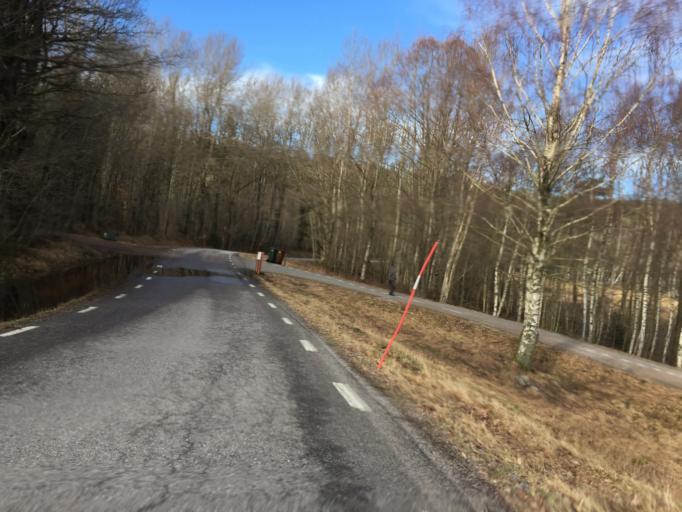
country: SE
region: Vaestra Goetaland
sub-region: Kungalvs Kommun
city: Kungalv
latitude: 57.9287
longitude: 11.9529
